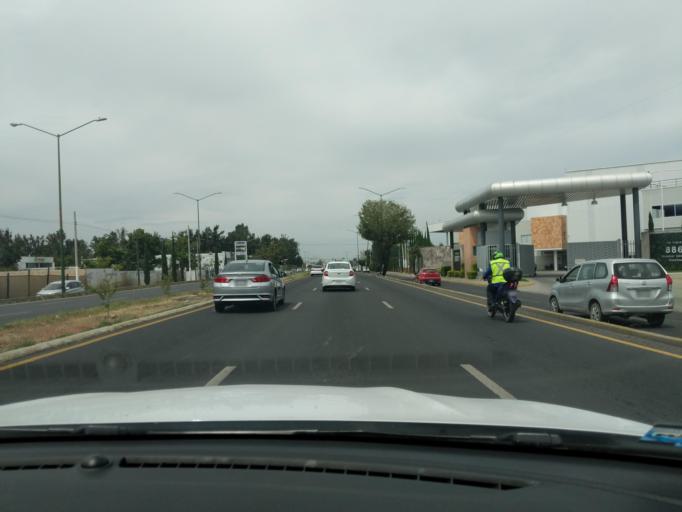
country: MX
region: Jalisco
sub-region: Zapopan
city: Puerta del Llano
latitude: 20.7846
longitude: -103.4683
